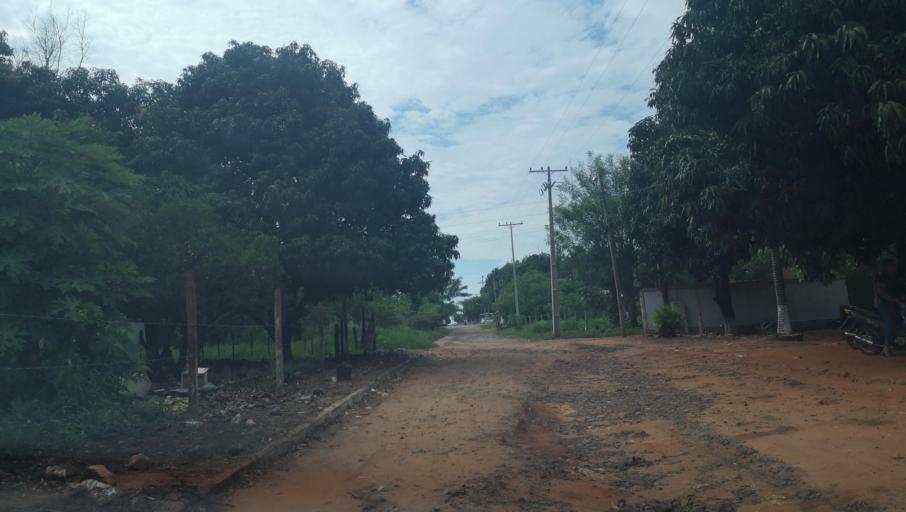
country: PY
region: San Pedro
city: Capiibary
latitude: -24.7230
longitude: -56.0183
